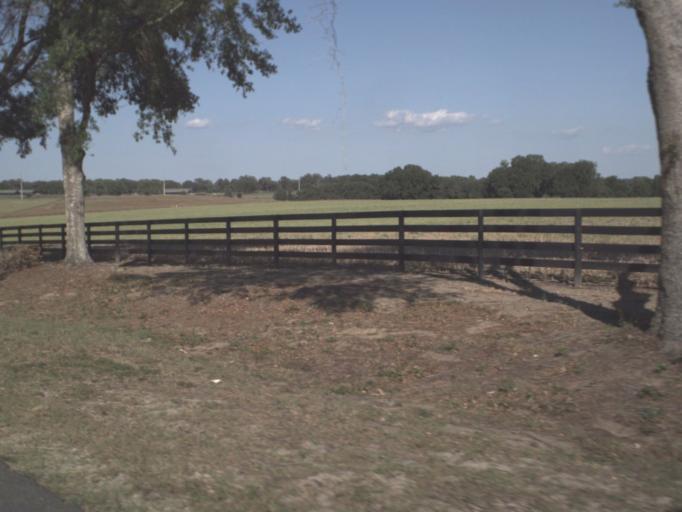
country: US
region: Florida
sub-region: Marion County
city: Dunnellon
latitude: 29.1530
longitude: -82.3612
